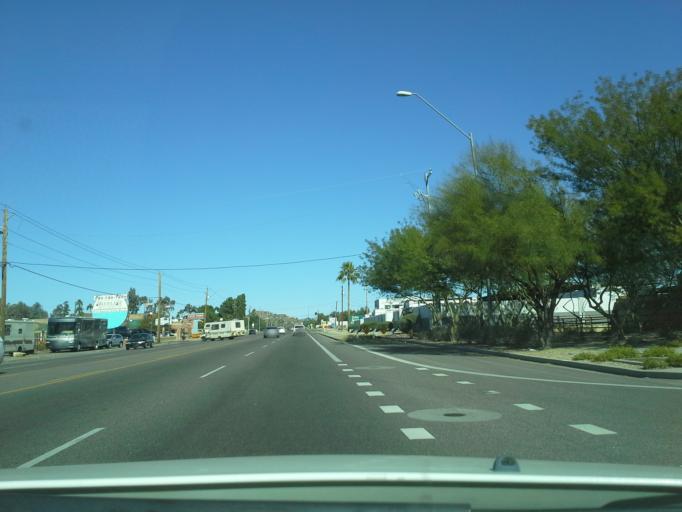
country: US
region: Arizona
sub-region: Maricopa County
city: Paradise Valley
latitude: 33.6436
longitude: -112.0308
